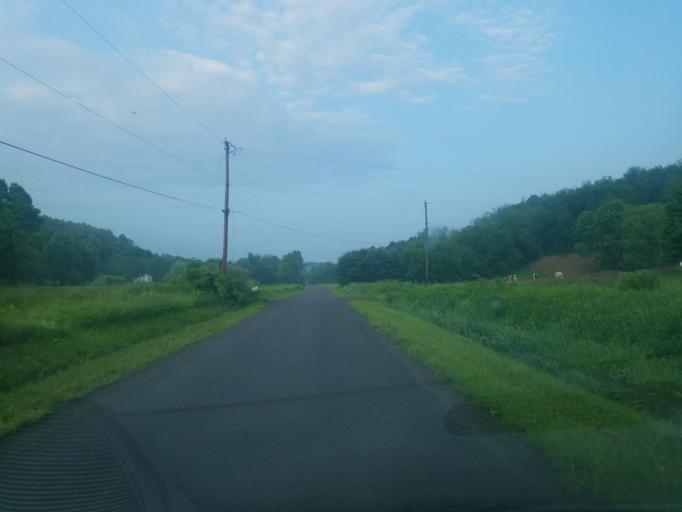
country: US
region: Ohio
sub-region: Stark County
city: Minerva
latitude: 40.7471
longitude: -80.9720
